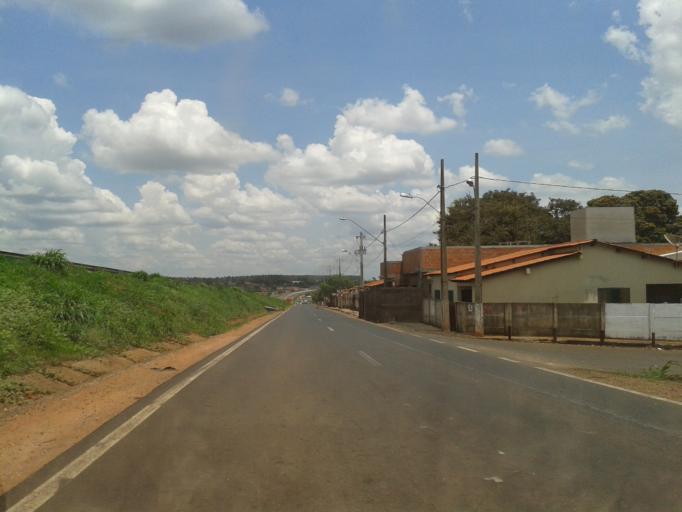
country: BR
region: Minas Gerais
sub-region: Monte Alegre De Minas
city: Monte Alegre de Minas
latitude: -18.8675
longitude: -48.8685
